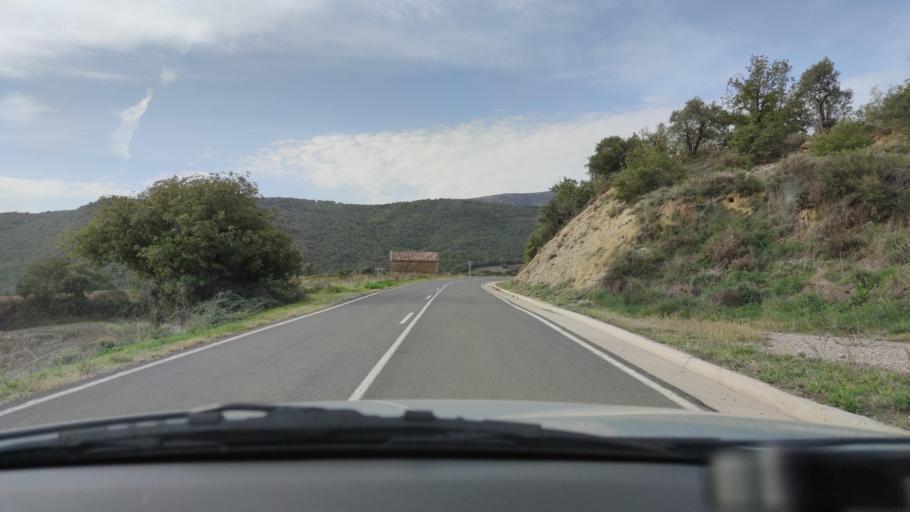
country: ES
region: Catalonia
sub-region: Provincia de Lleida
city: Artesa de Segre
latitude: 41.9924
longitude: 1.0056
